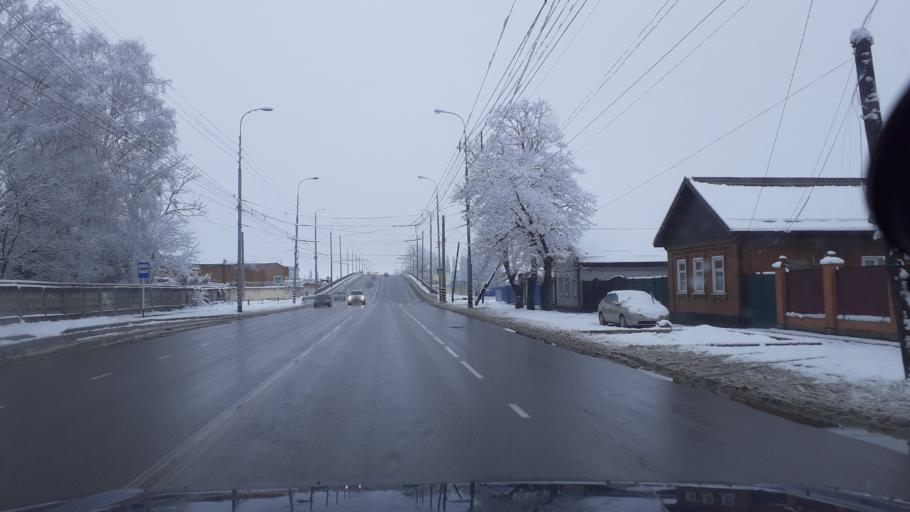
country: RU
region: Adygeya
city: Maykop
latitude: 44.6185
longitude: 40.1212
